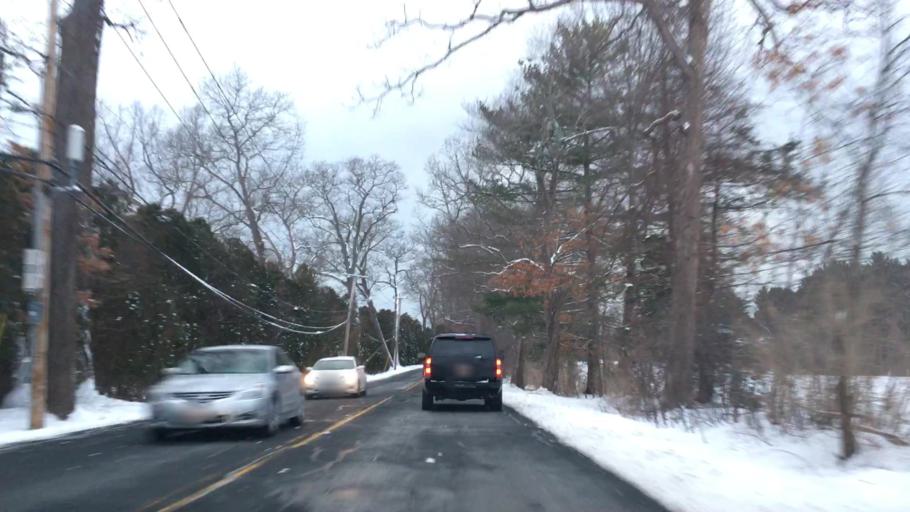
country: US
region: Massachusetts
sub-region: Hampden County
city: Longmeadow
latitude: 42.0394
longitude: -72.5673
